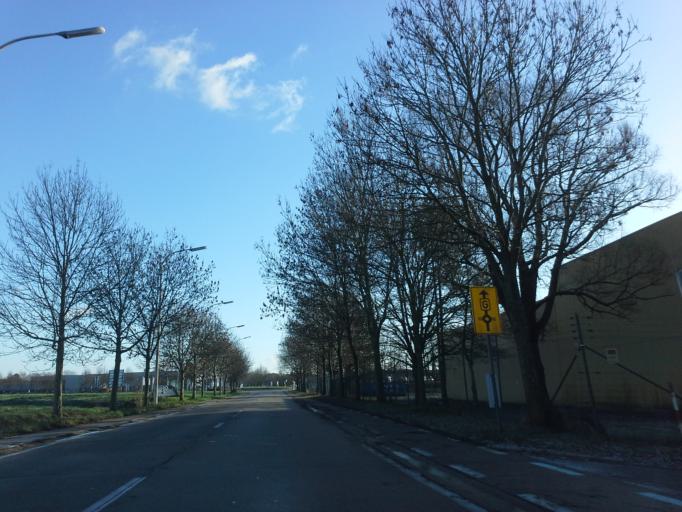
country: BE
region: Flanders
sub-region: Provincie Antwerpen
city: Herentals
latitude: 51.1623
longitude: 4.8051
